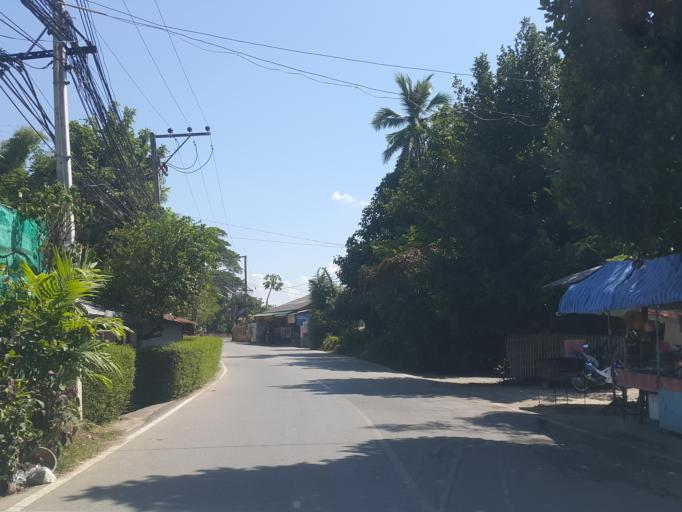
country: TH
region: Chiang Mai
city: Saraphi
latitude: 18.7680
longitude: 99.0440
